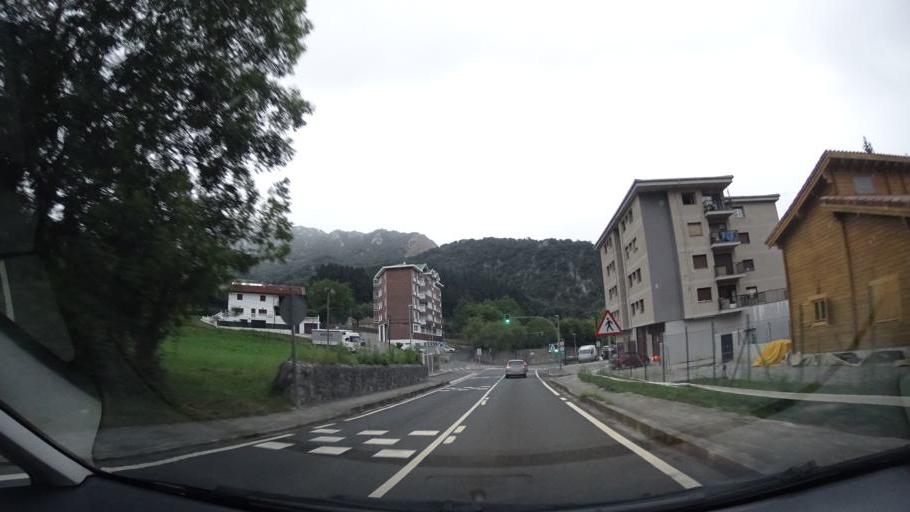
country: ES
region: Basque Country
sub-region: Bizkaia
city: Manaria
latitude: 43.1362
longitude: -2.6620
